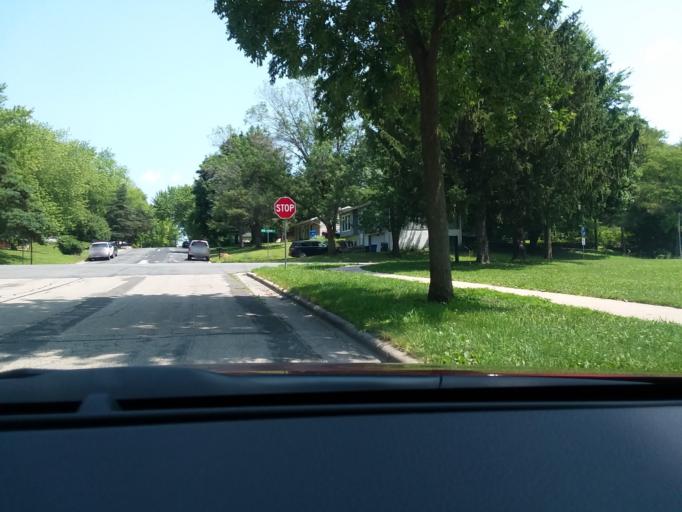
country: US
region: Wisconsin
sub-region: Dane County
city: Shorewood Hills
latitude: 43.0290
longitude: -89.4566
